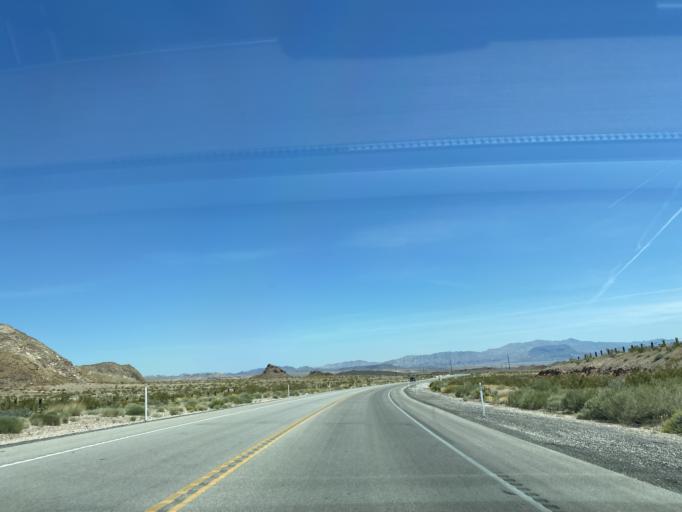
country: US
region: Nevada
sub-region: Clark County
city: Nellis Air Force Base
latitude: 36.2063
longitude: -114.9482
